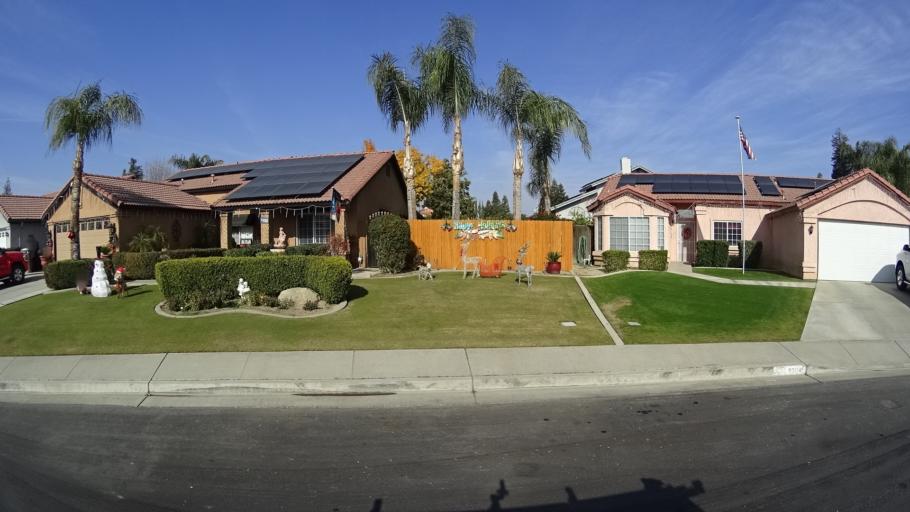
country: US
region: California
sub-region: Kern County
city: Greenacres
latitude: 35.3661
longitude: -119.1030
